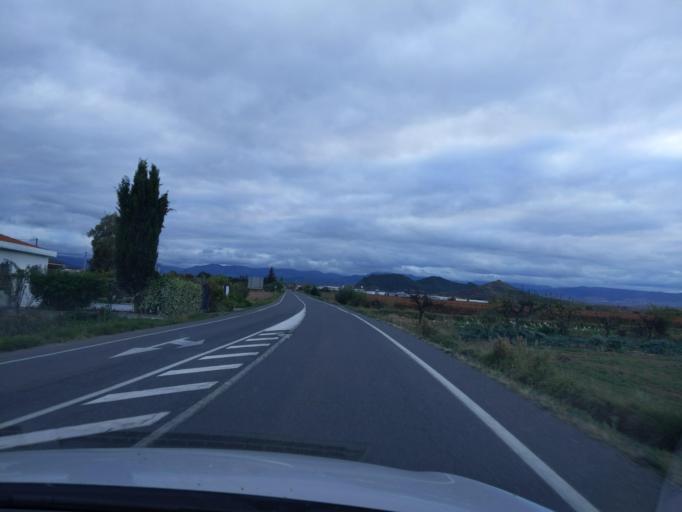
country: ES
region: La Rioja
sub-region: Provincia de La Rioja
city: Urunuela
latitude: 42.4343
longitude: -2.7139
